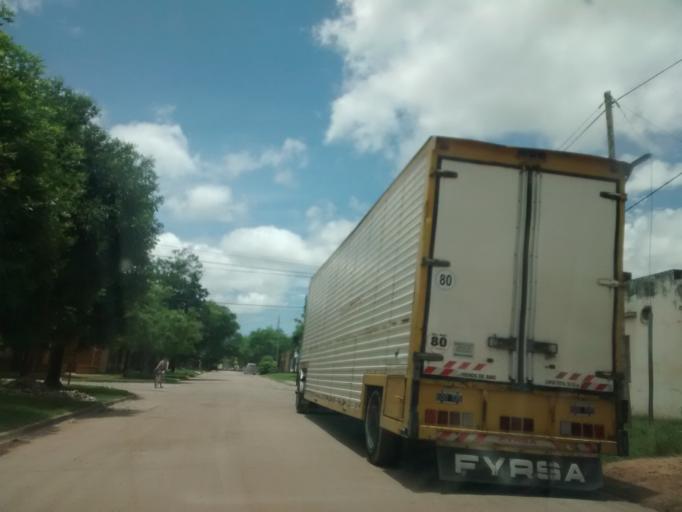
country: AR
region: Chaco
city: Fontana
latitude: -27.4366
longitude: -59.0047
